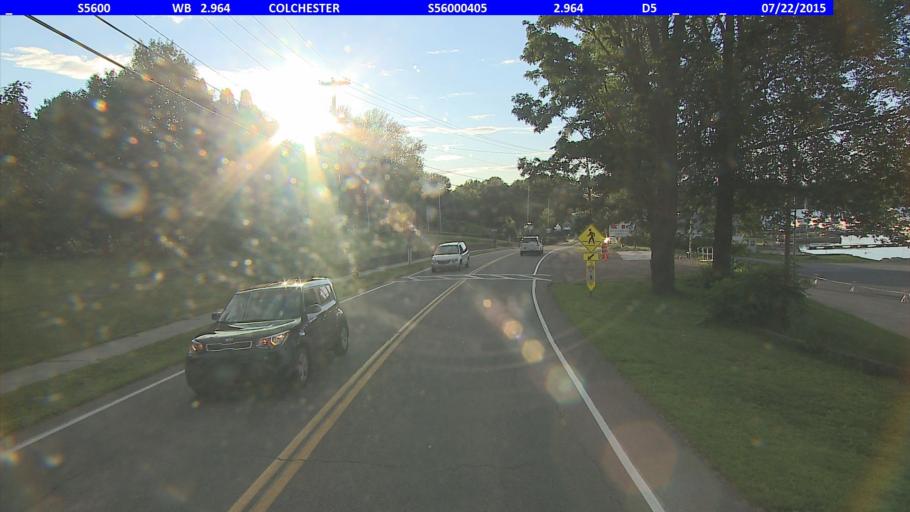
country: US
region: Vermont
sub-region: Chittenden County
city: Winooski
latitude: 44.5464
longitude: -73.2200
